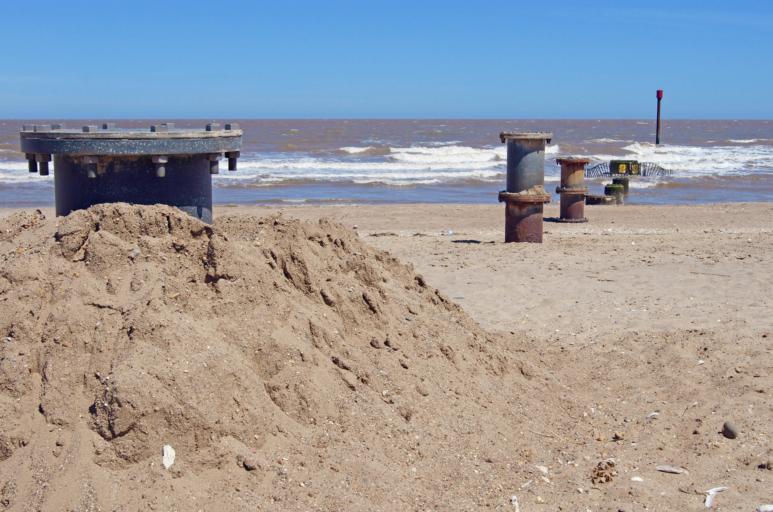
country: GB
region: England
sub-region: Lincolnshire
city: Mablethorpe
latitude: 53.2944
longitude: 0.3001
